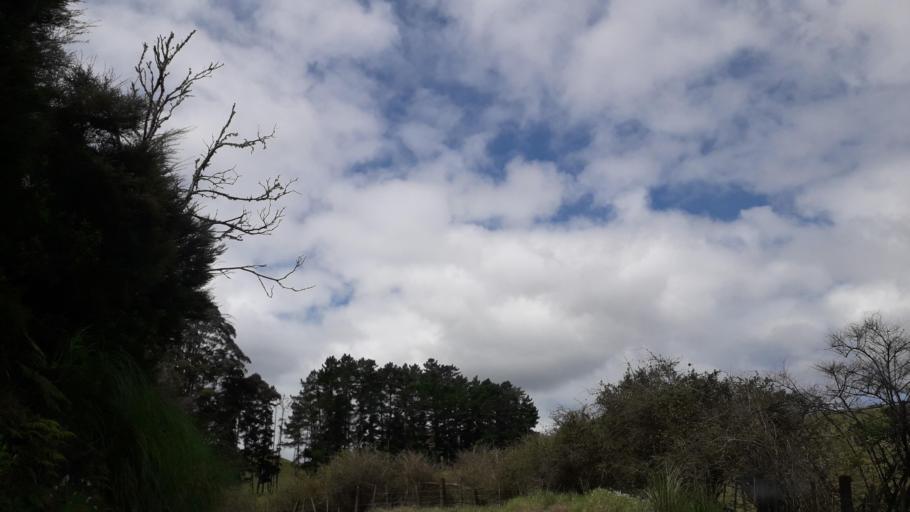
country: NZ
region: Northland
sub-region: Far North District
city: Taipa
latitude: -35.0933
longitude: 173.5211
